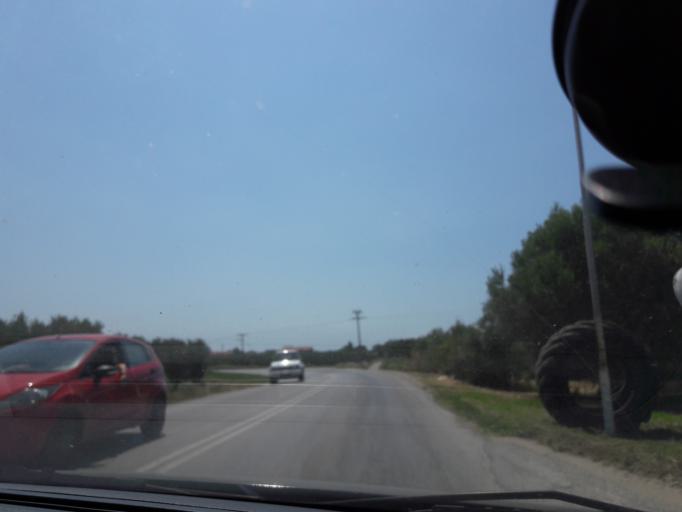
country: GR
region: Central Macedonia
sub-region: Nomos Chalkidikis
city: Nea Kallikrateia
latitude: 40.3301
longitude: 23.0609
